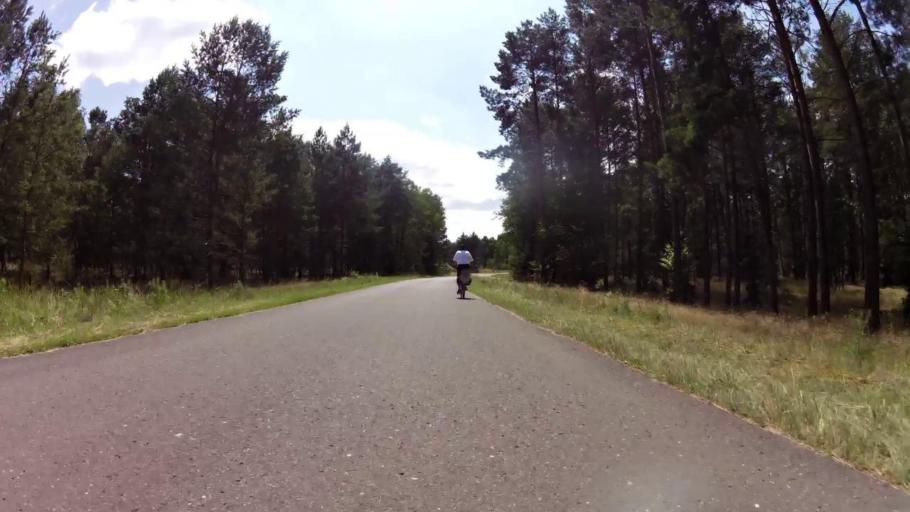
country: PL
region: West Pomeranian Voivodeship
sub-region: Powiat choszczenski
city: Drawno
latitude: 53.3791
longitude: 15.7290
